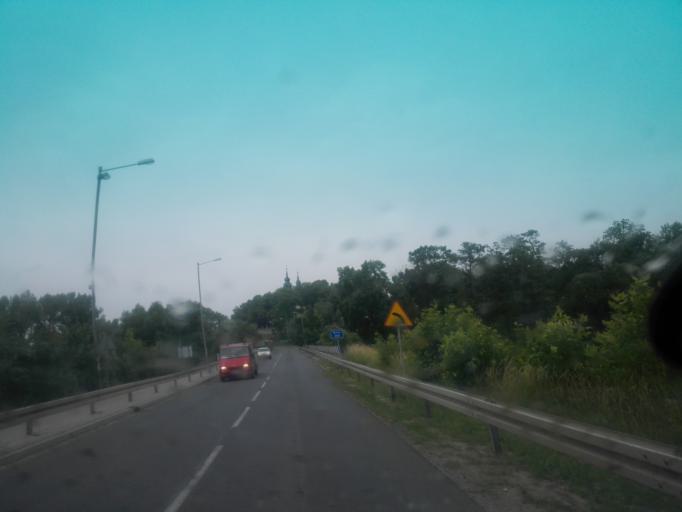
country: PL
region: Silesian Voivodeship
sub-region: Powiat czestochowski
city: Mstow
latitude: 50.8298
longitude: 19.2901
